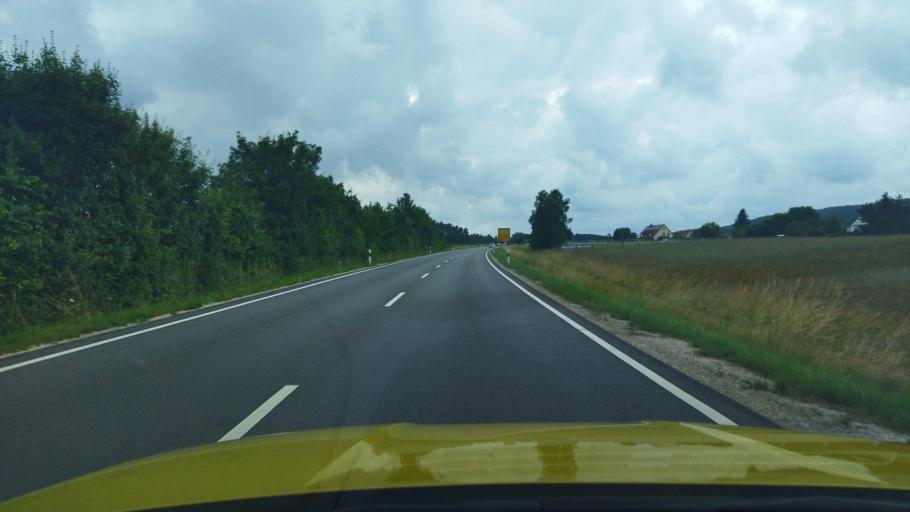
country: DE
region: Bavaria
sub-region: Regierungsbezirk Mittelfranken
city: Absberg
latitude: 49.1089
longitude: 10.9165
